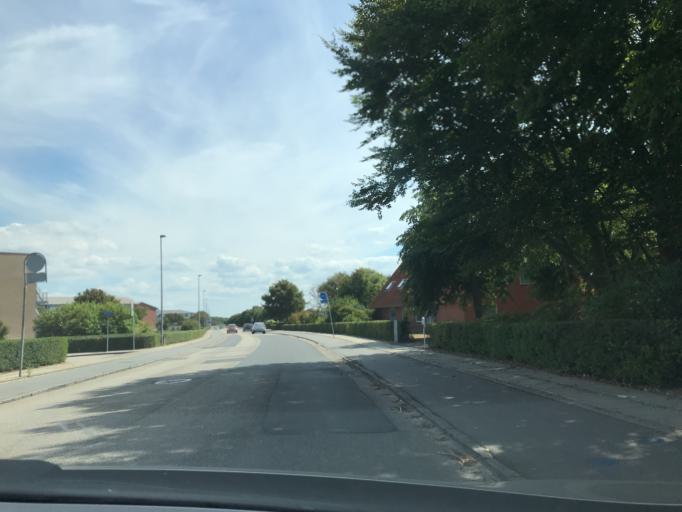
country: DK
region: Central Jutland
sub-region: Ringkobing-Skjern Kommune
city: Ringkobing
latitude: 56.0818
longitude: 8.2580
